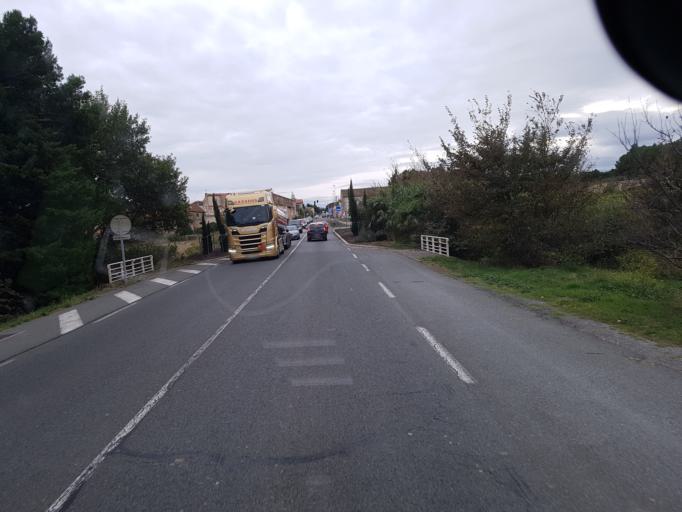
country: FR
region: Languedoc-Roussillon
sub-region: Departement de l'Aude
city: Peyriac-de-Mer
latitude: 43.1215
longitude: 2.9545
